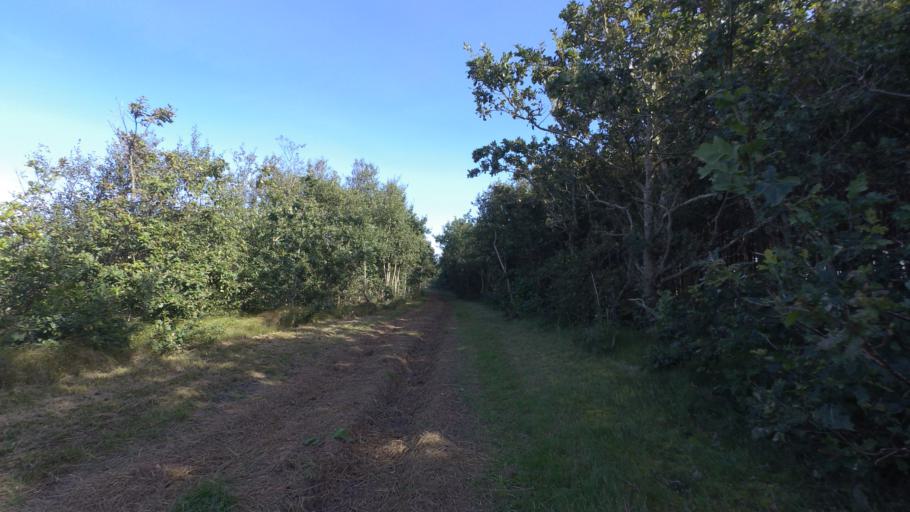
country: NL
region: Friesland
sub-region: Gemeente Ameland
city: Nes
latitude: 53.4468
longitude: 5.7076
